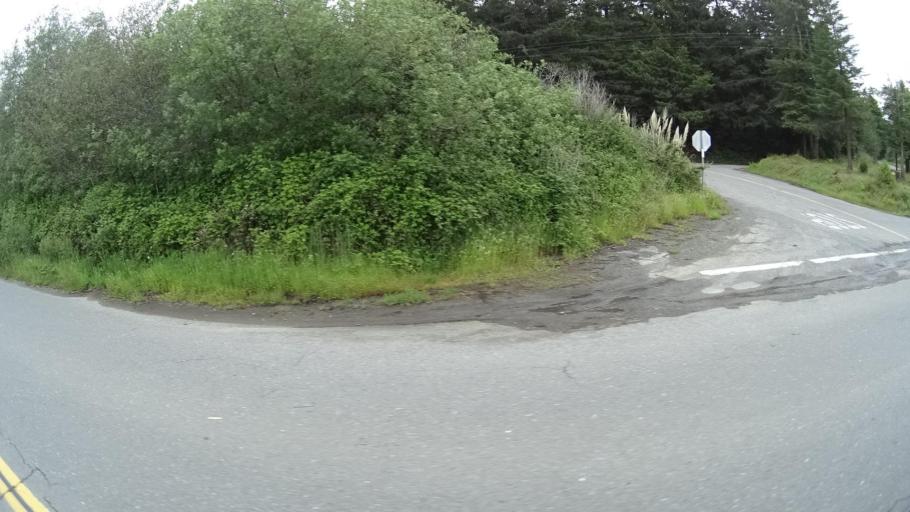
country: US
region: California
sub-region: Humboldt County
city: Blue Lake
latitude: 40.8775
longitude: -123.9796
